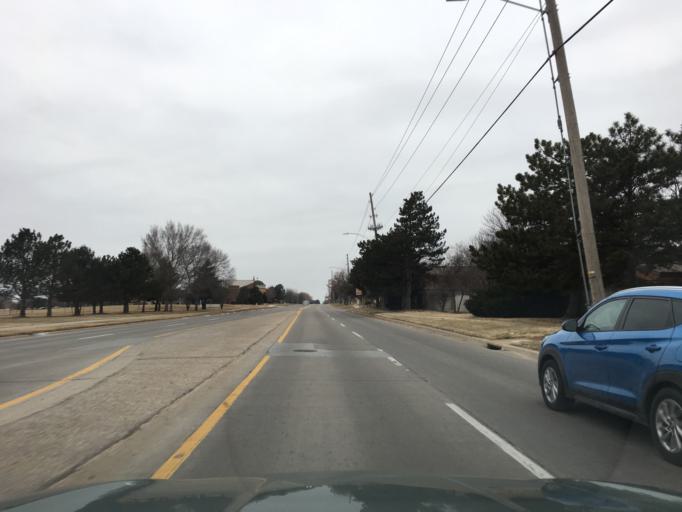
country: US
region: Kansas
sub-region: Sedgwick County
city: Bellaire
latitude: 37.7085
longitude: -97.2452
